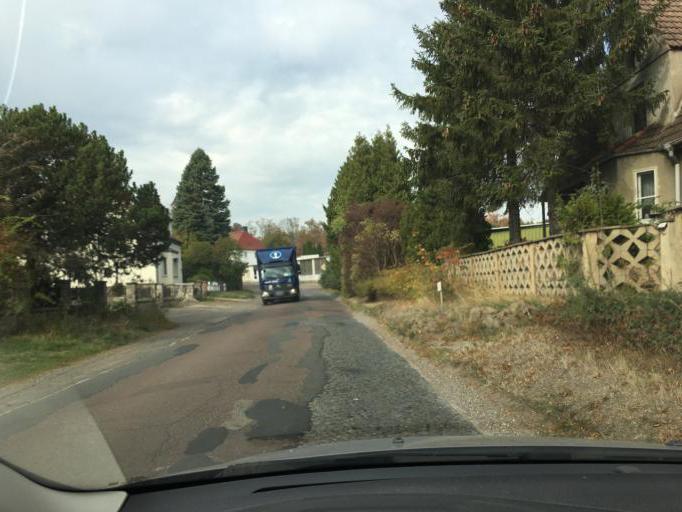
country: DE
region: Saxony-Anhalt
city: Landsberg
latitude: 51.5231
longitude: 12.1668
